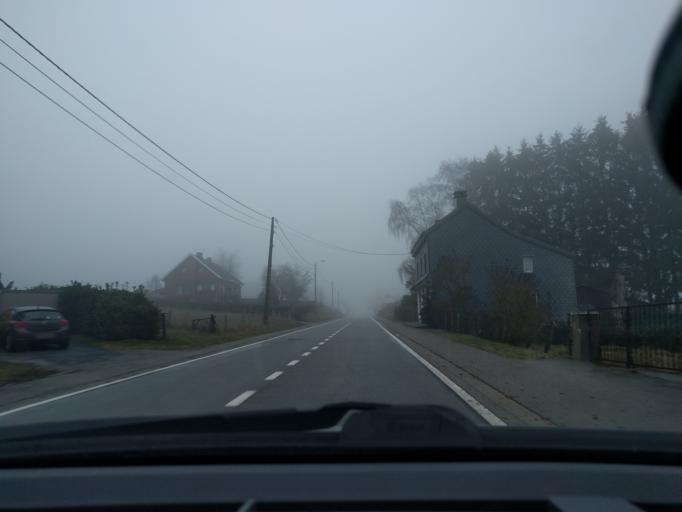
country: BE
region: Wallonia
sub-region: Province du Luxembourg
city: Gouvy
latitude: 50.1919
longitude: 5.9592
